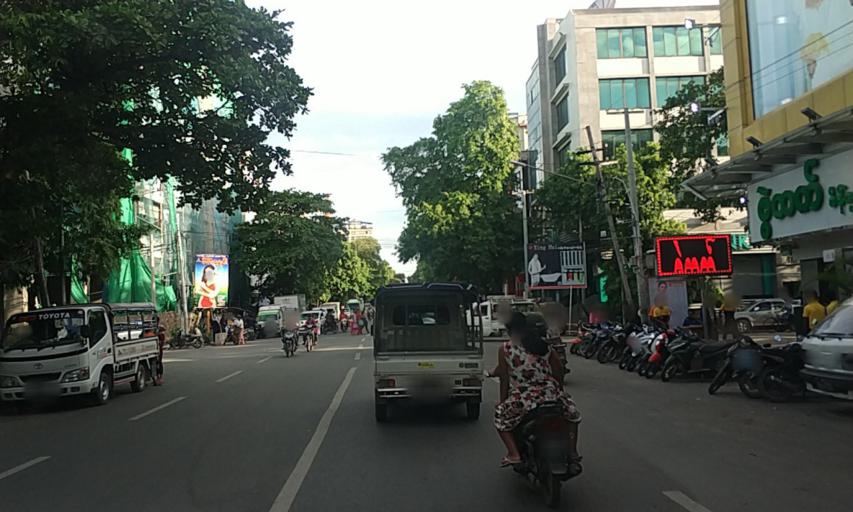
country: MM
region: Mandalay
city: Mandalay
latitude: 21.9777
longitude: 96.0776
